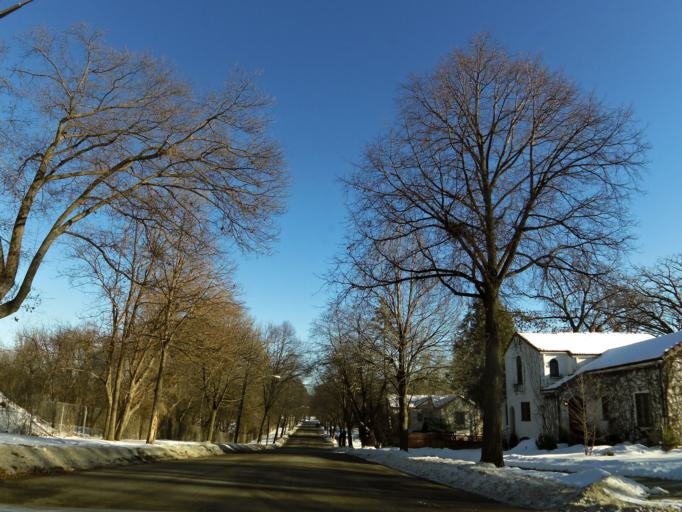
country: US
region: Minnesota
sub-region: Hennepin County
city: Saint Louis Park
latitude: 44.9341
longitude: -93.3279
